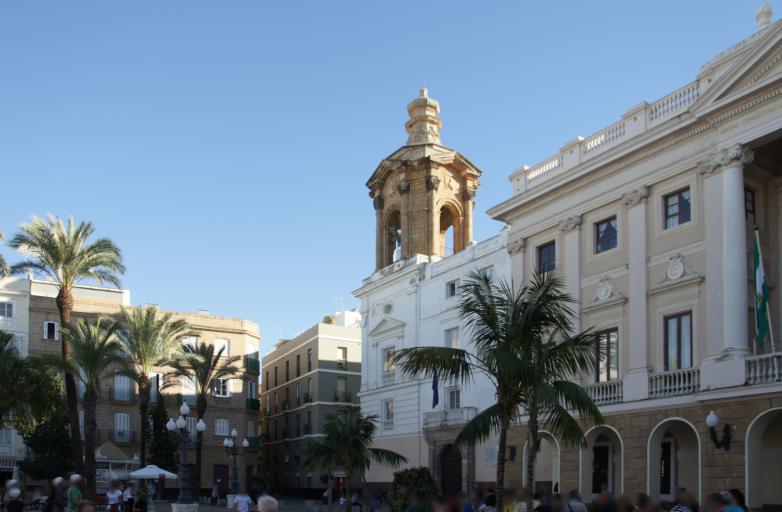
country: ES
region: Andalusia
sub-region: Provincia de Cadiz
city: Cadiz
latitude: 36.5300
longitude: -6.2929
